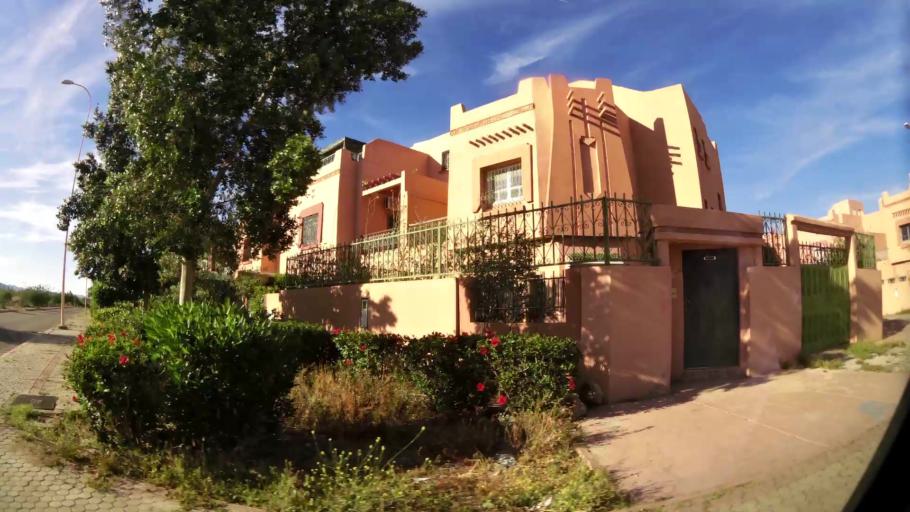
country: MA
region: Marrakech-Tensift-Al Haouz
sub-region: Marrakech
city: Marrakesh
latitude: 31.7510
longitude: -8.1082
